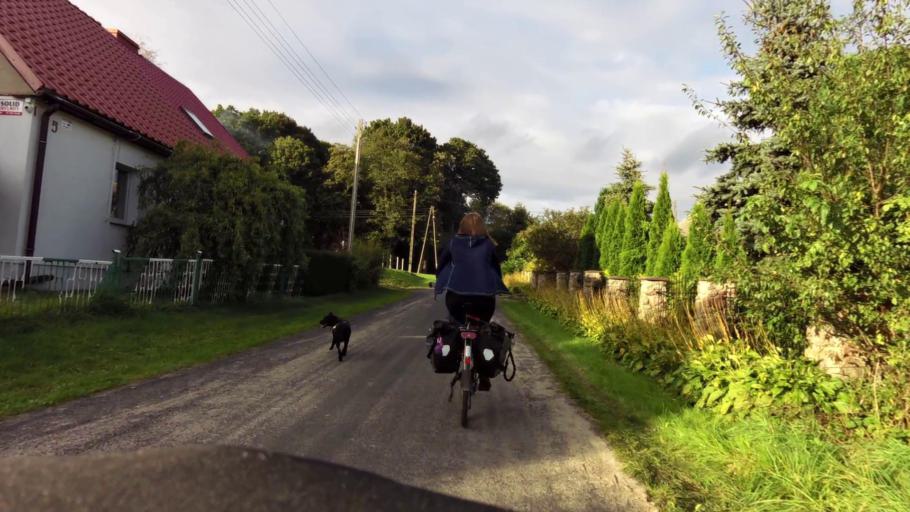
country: PL
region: West Pomeranian Voivodeship
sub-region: Powiat stargardzki
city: Dobrzany
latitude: 53.3851
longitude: 15.3592
